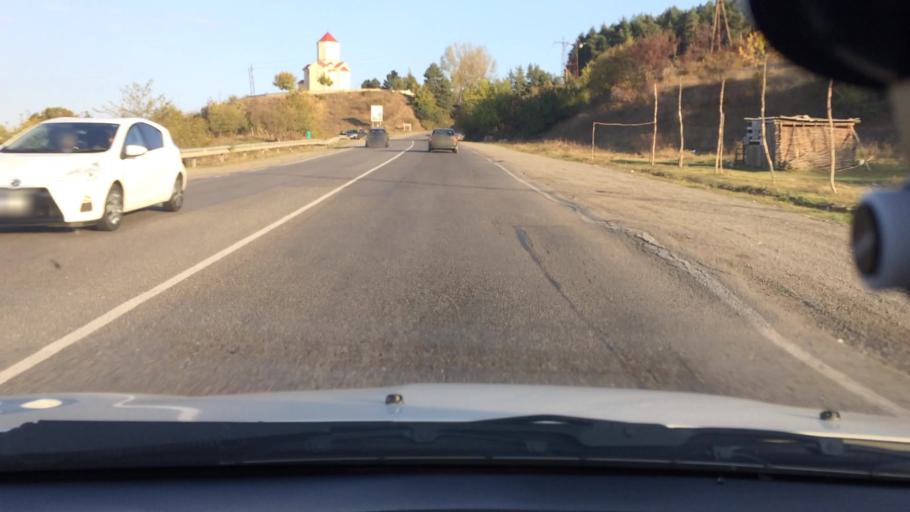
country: GE
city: Surami
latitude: 42.0185
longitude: 43.5668
